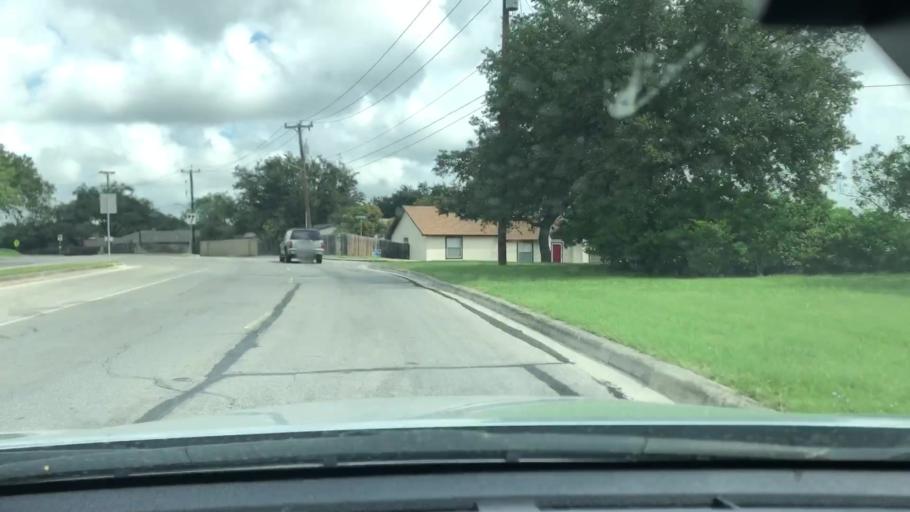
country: US
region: Texas
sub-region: Bexar County
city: Windcrest
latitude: 29.5162
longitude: -98.3700
